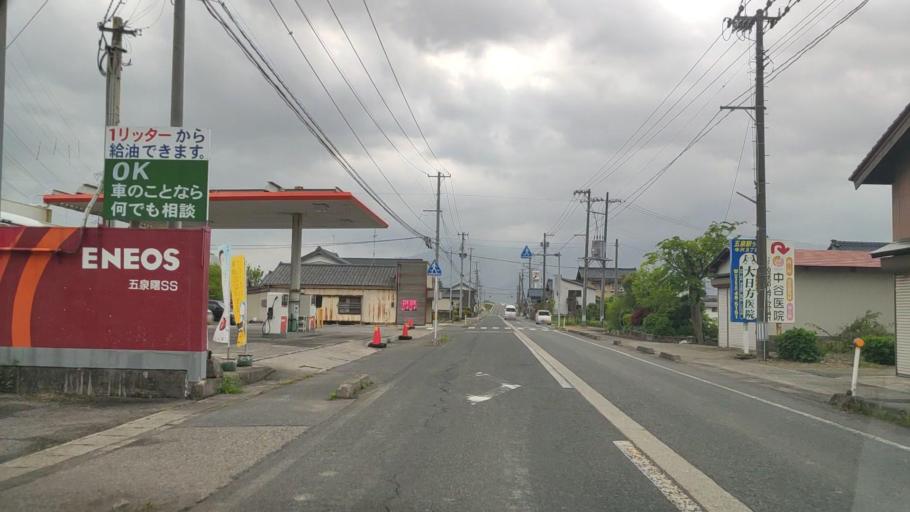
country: JP
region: Niigata
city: Gosen
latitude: 37.7339
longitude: 139.1970
